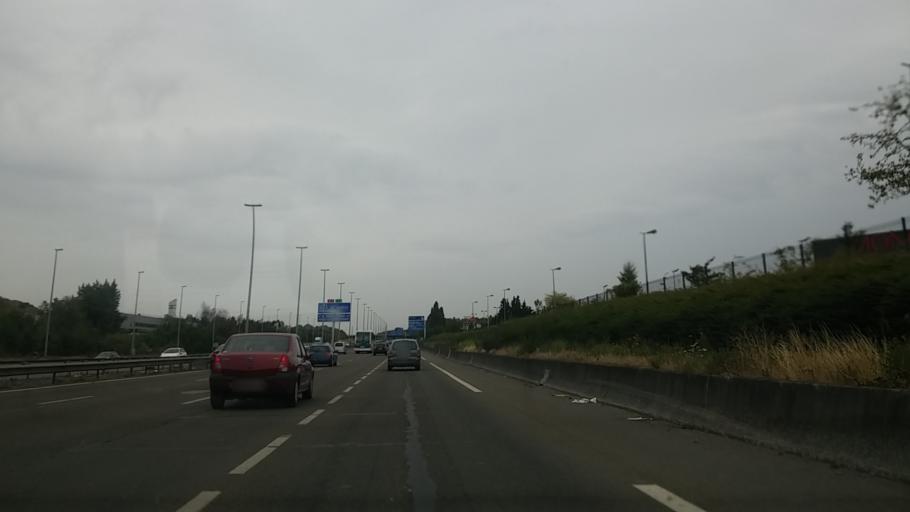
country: FR
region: Ile-de-France
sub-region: Departement de Seine-Saint-Denis
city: Le Blanc-Mesnil
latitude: 48.9558
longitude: 2.4593
